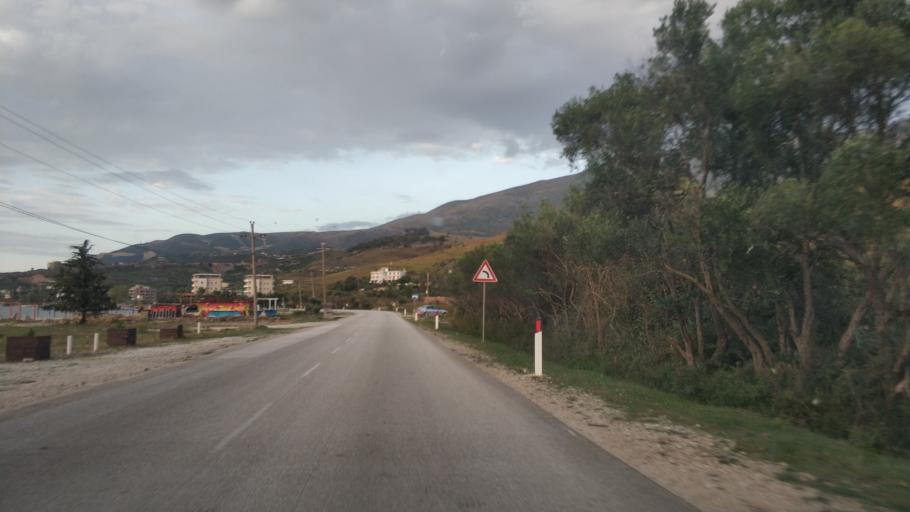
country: AL
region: Vlore
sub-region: Rrethi i Vlores
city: Orikum
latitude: 40.3460
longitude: 19.4847
